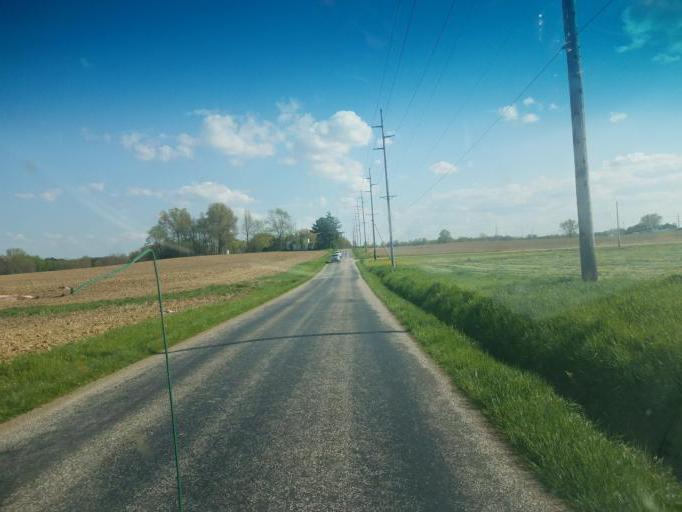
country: US
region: Ohio
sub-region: Wayne County
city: Smithville
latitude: 40.8327
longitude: -81.8776
